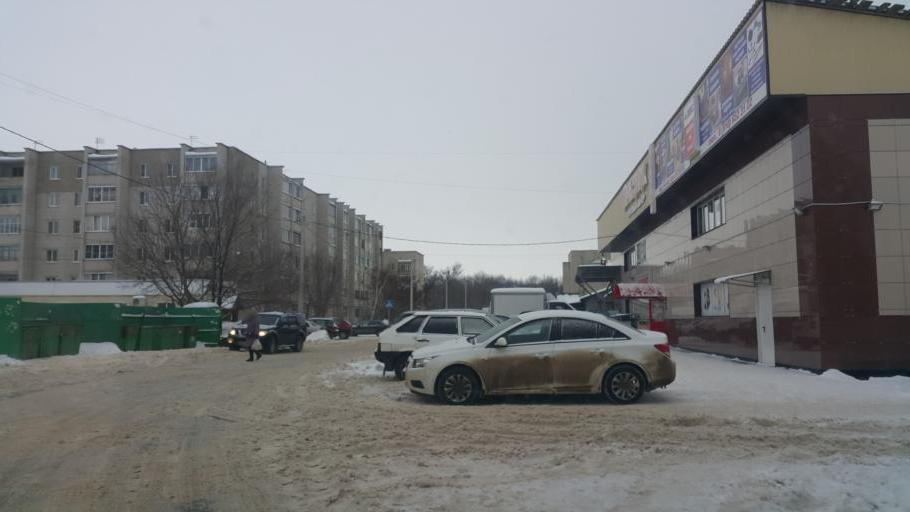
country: RU
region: Tambov
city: Bokino
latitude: 52.6420
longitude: 41.4451
